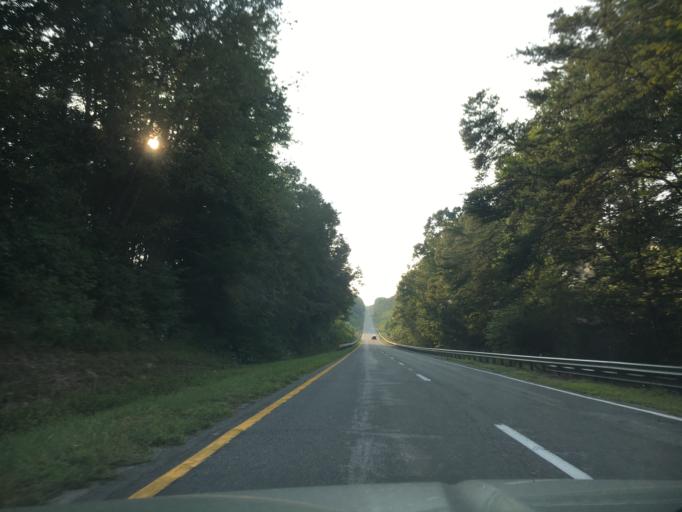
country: US
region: Virginia
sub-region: Appomattox County
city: Appomattox
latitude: 37.2700
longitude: -78.6672
